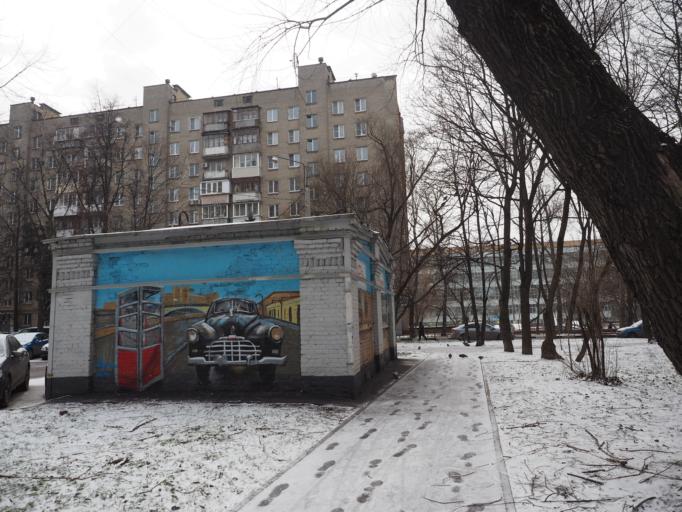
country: RU
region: Moscow
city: Novyye Cheremushki
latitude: 55.6826
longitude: 37.5920
